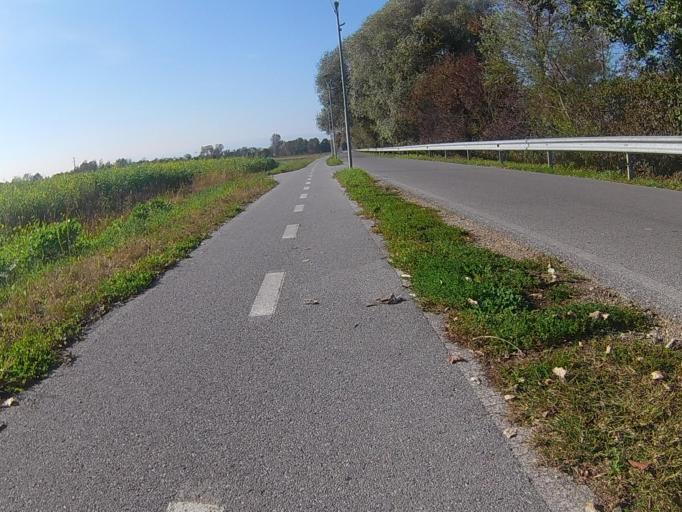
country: SI
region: Hajdina
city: Spodnja Hajdina
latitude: 46.4265
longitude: 15.8468
